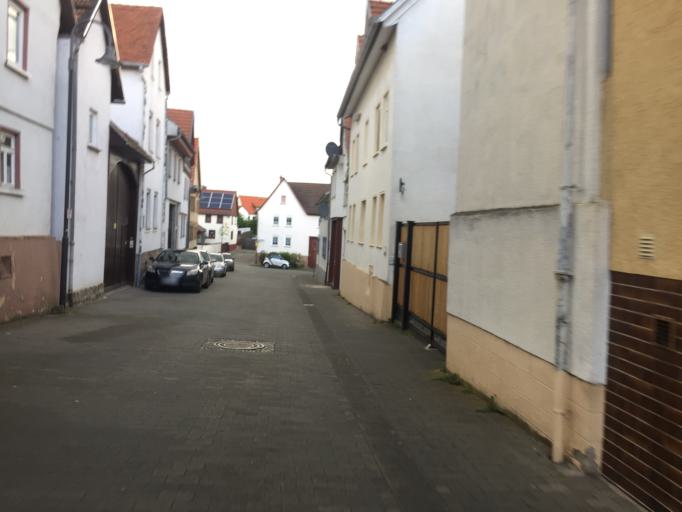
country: DE
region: Hesse
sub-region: Regierungsbezirk Darmstadt
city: Rockenberg
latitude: 50.4399
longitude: 8.7045
